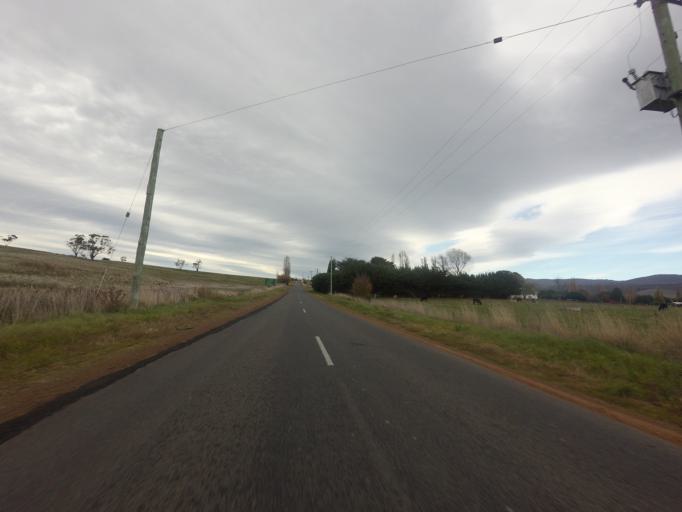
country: AU
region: Tasmania
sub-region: Derwent Valley
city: New Norfolk
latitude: -42.5327
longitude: 146.7524
